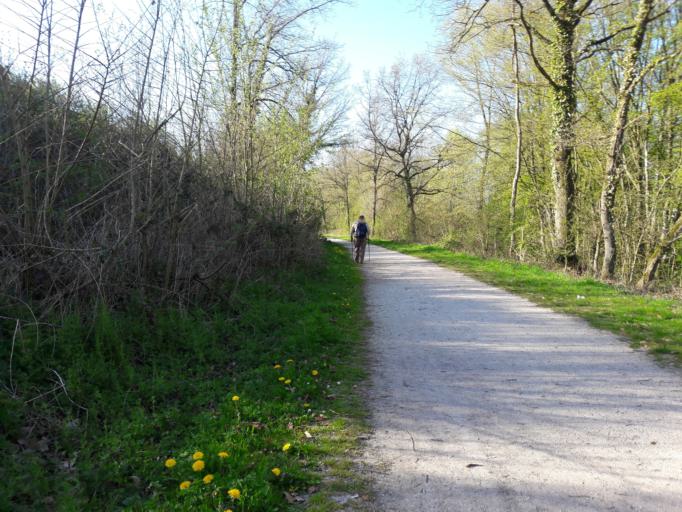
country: FR
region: Nord-Pas-de-Calais
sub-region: Departement du Nord
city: Ferriere-la-Grande
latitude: 50.2489
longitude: 4.0078
